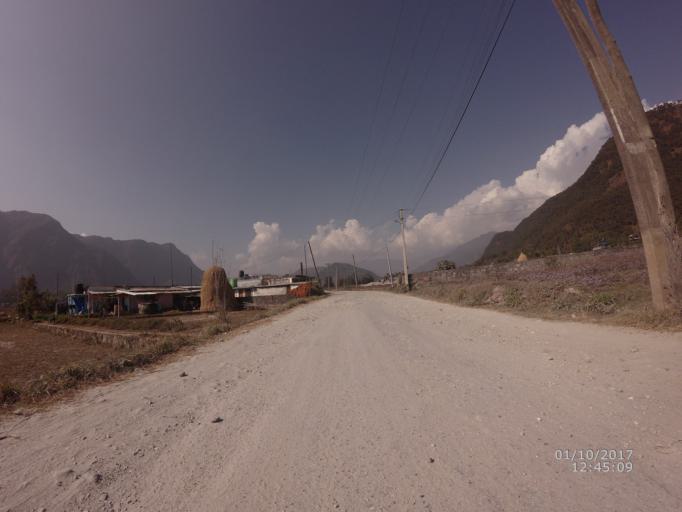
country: NP
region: Western Region
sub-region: Gandaki Zone
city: Pokhara
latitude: 28.2696
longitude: 83.9609
